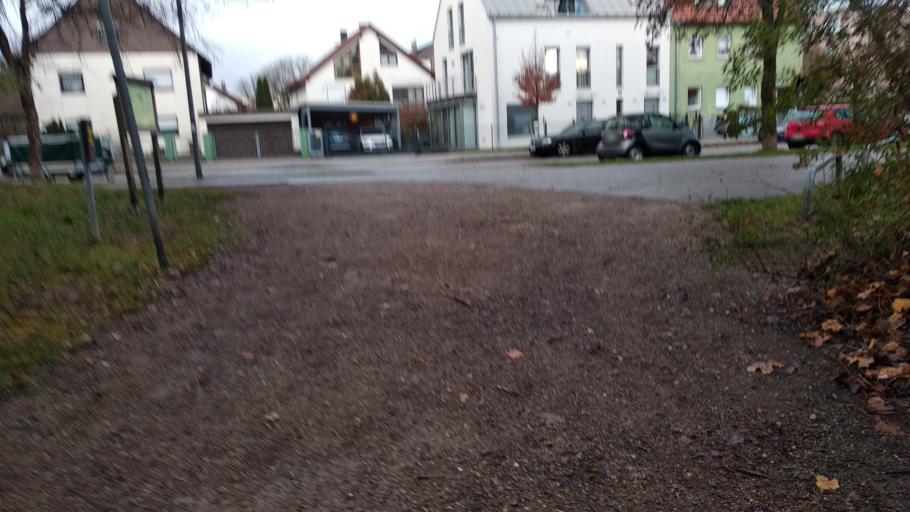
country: DE
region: Bavaria
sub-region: Upper Bavaria
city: Neubiberg
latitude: 48.1038
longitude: 11.6328
